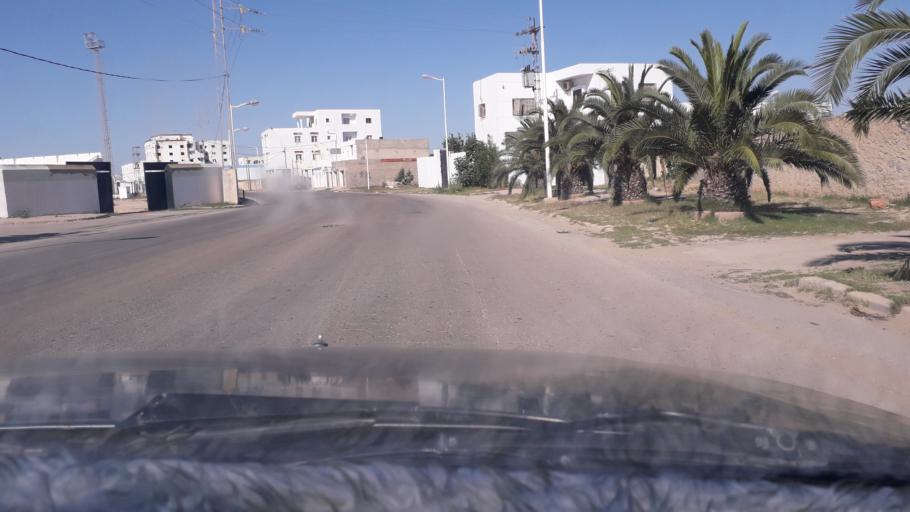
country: TN
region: Safaqis
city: Al Qarmadah
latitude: 34.8447
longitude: 10.7591
